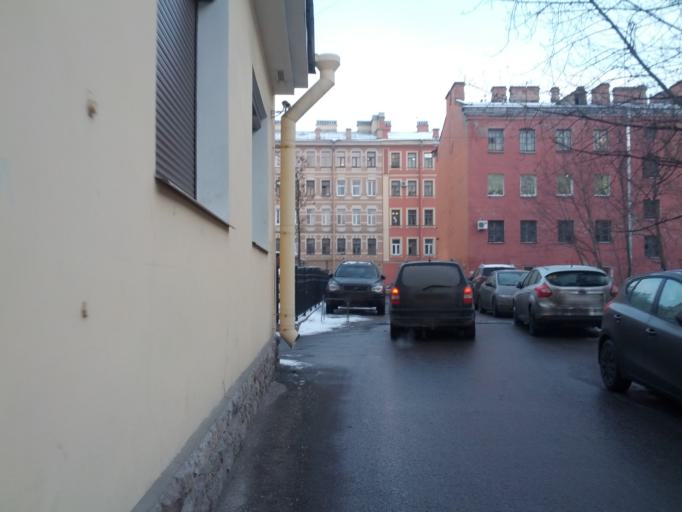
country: RU
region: St.-Petersburg
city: Centralniy
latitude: 59.9138
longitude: 30.3451
